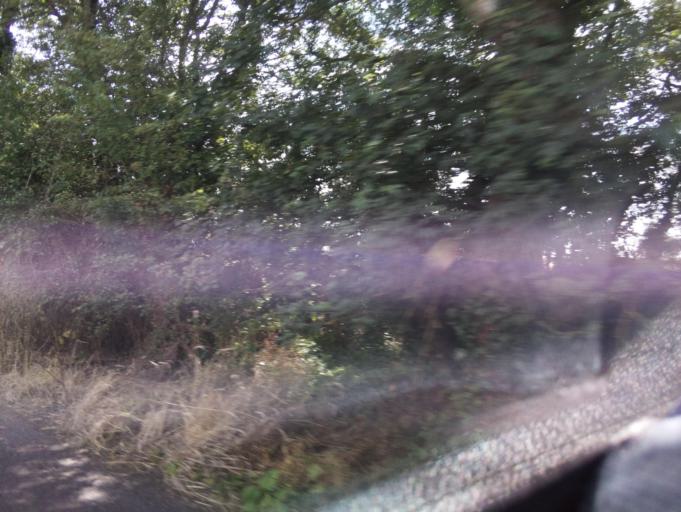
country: GB
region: England
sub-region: Wiltshire
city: Hankerton
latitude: 51.6240
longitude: -2.0608
